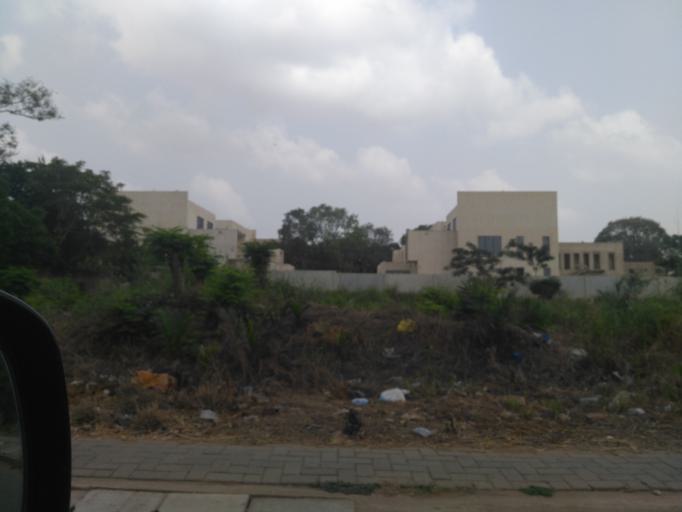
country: GH
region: Greater Accra
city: Accra
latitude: 5.6054
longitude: -0.1796
